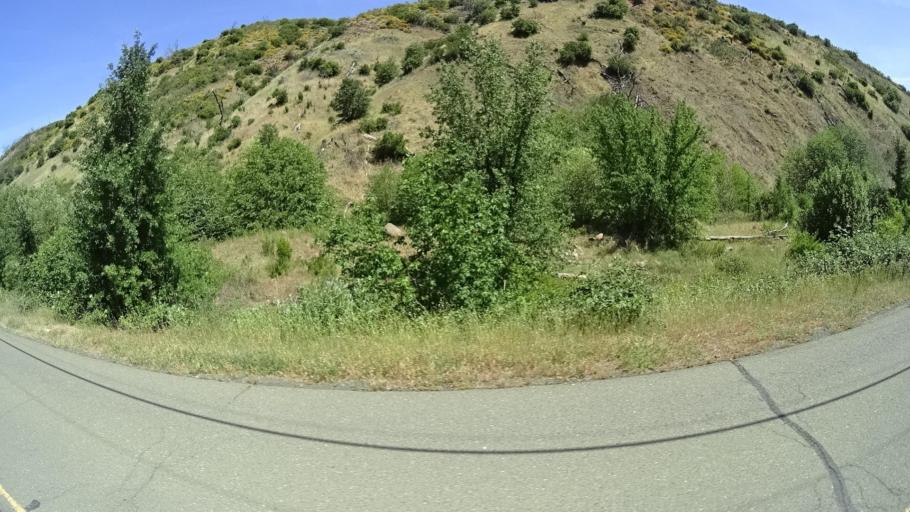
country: US
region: California
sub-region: Lake County
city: Middletown
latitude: 38.7786
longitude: -122.6398
